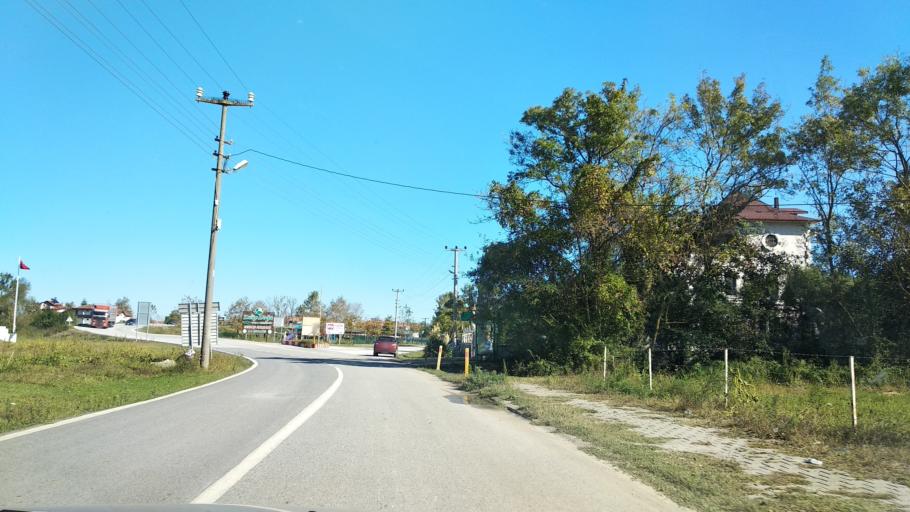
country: TR
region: Sakarya
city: Karasu
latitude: 41.1187
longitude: 30.6427
